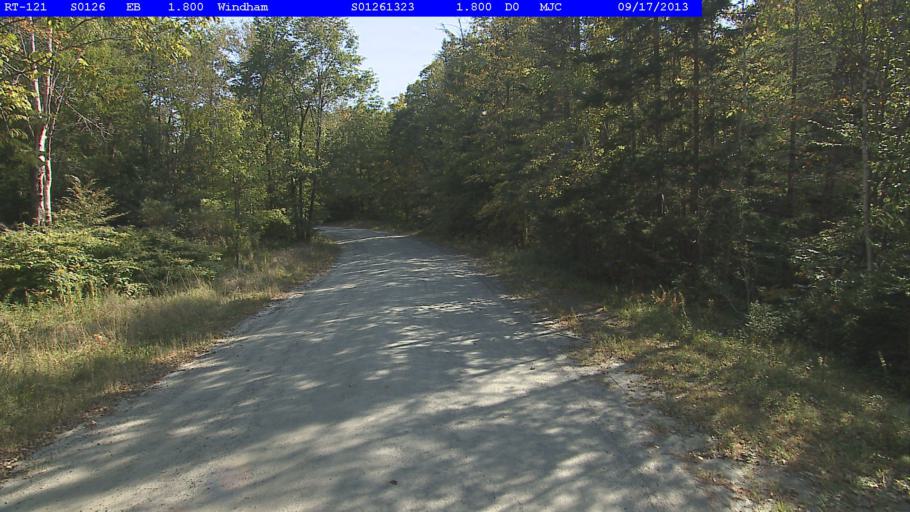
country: US
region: Vermont
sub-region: Windsor County
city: Chester
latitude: 43.1955
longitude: -72.6872
